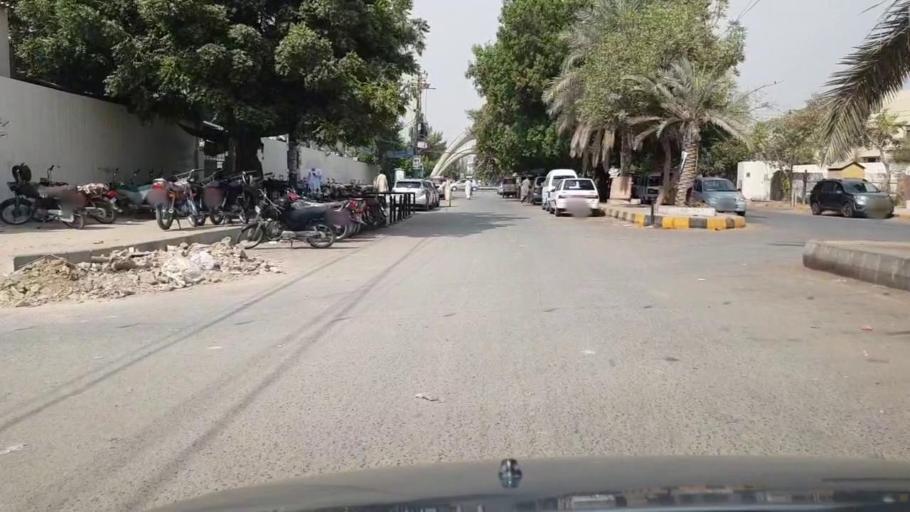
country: PK
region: Sindh
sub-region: Karachi District
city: Karachi
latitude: 24.8751
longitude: 67.0858
